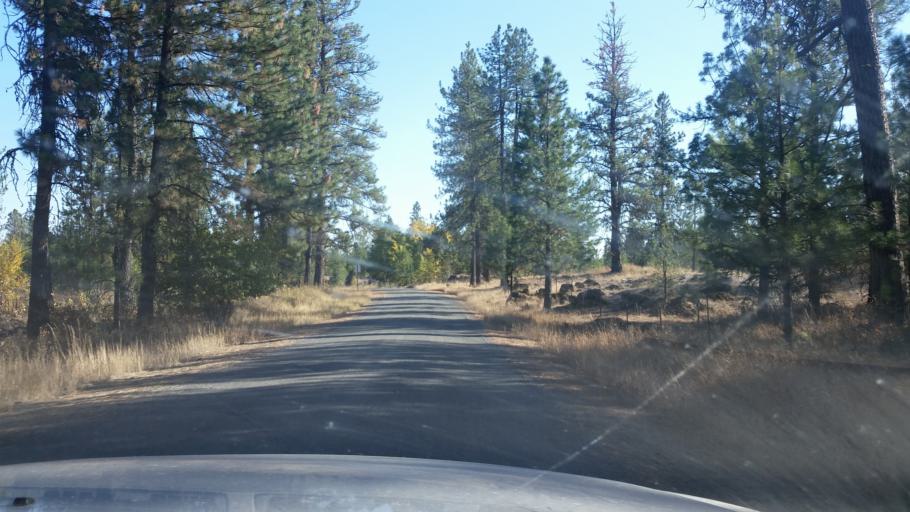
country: US
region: Washington
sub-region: Spokane County
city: Cheney
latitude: 47.4168
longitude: -117.6485
